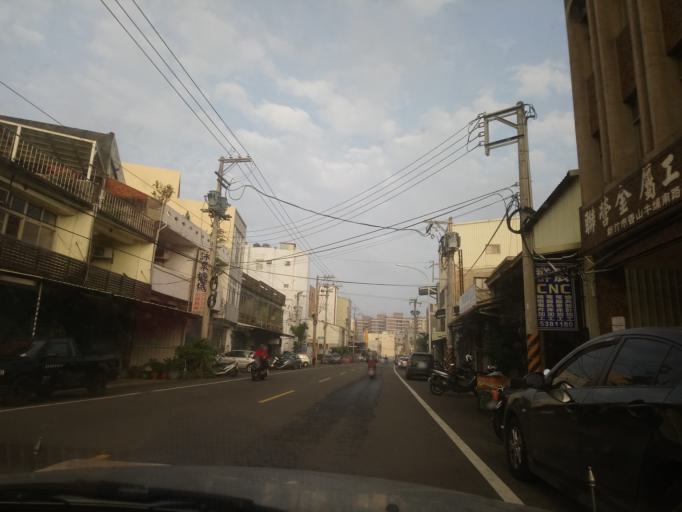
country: TW
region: Taiwan
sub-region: Hsinchu
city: Hsinchu
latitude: 24.7959
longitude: 120.9347
